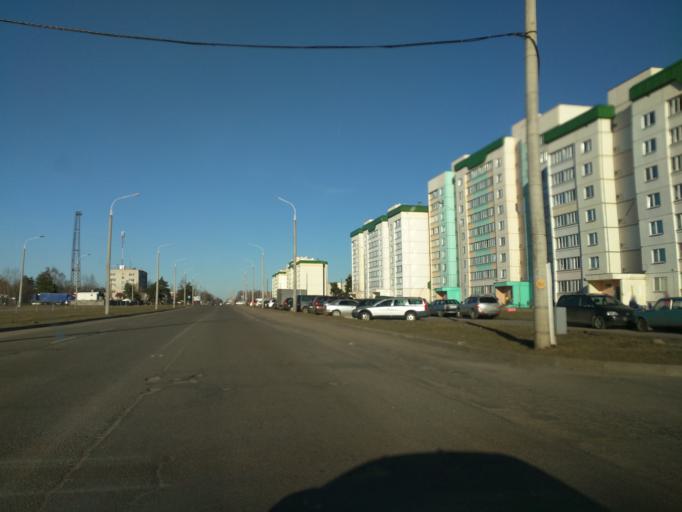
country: BY
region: Mogilev
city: Babruysk
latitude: 53.1678
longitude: 29.1651
